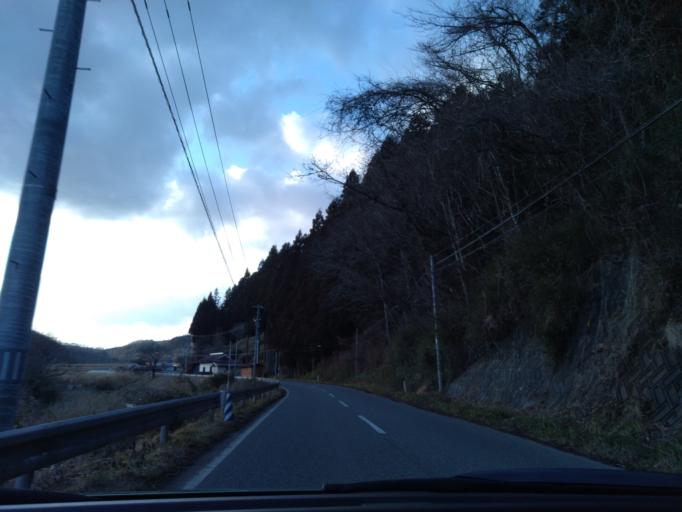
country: JP
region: Iwate
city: Ichinoseki
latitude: 38.9107
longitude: 141.0588
